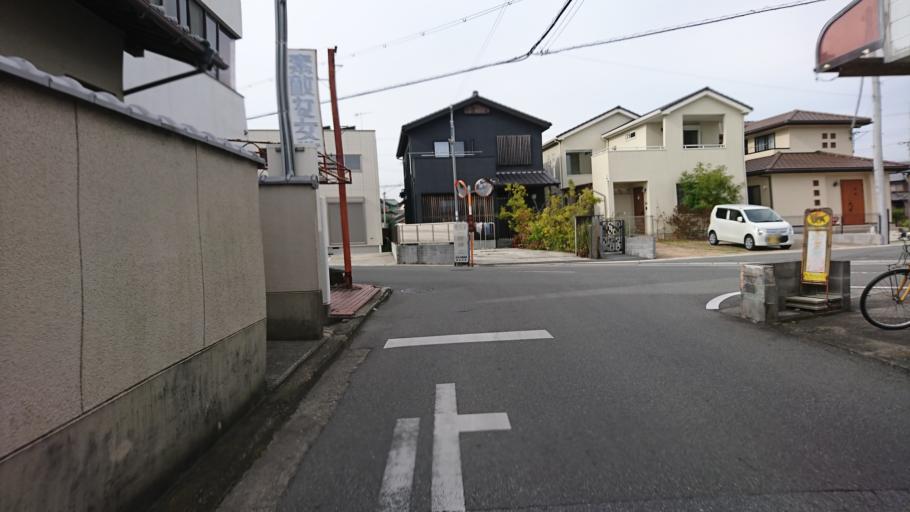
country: JP
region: Hyogo
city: Kakogawacho-honmachi
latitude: 34.7894
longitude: 134.8813
